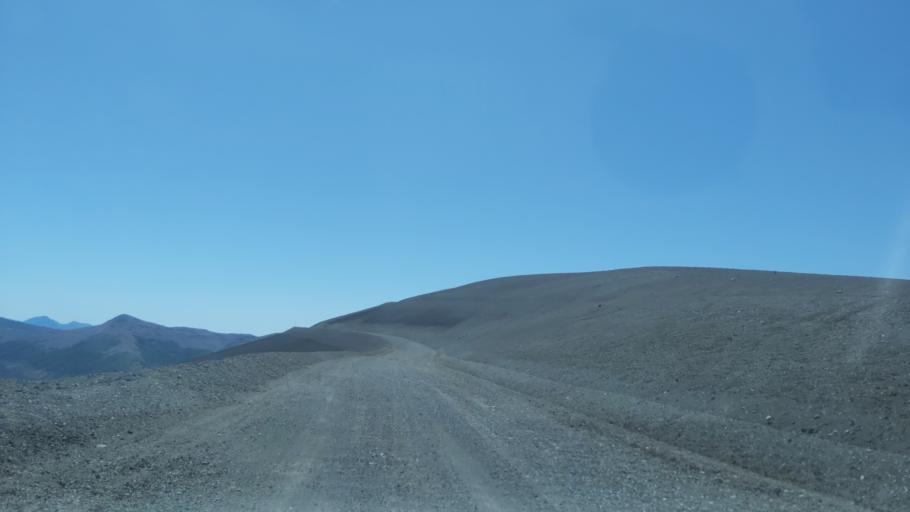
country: CL
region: Araucania
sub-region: Provincia de Cautin
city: Vilcun
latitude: -38.3728
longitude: -71.5389
